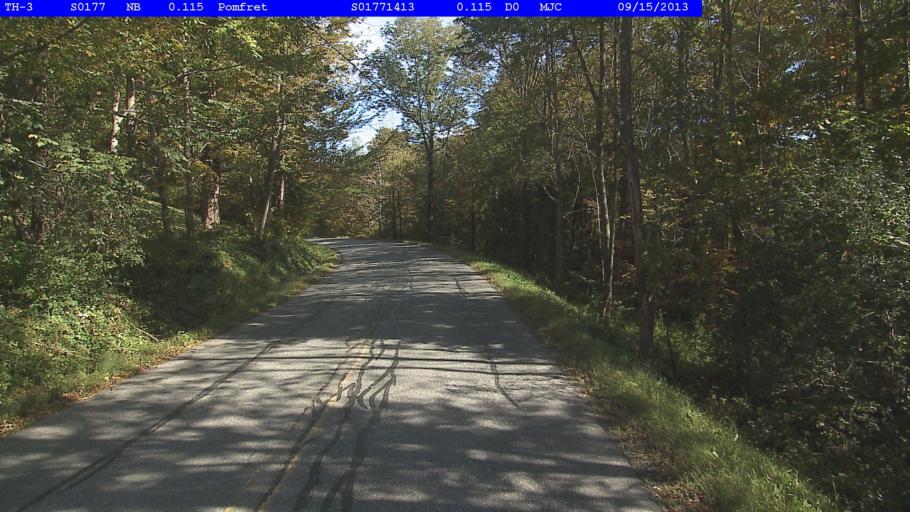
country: US
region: Vermont
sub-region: Windsor County
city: Woodstock
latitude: 43.7246
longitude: -72.4977
